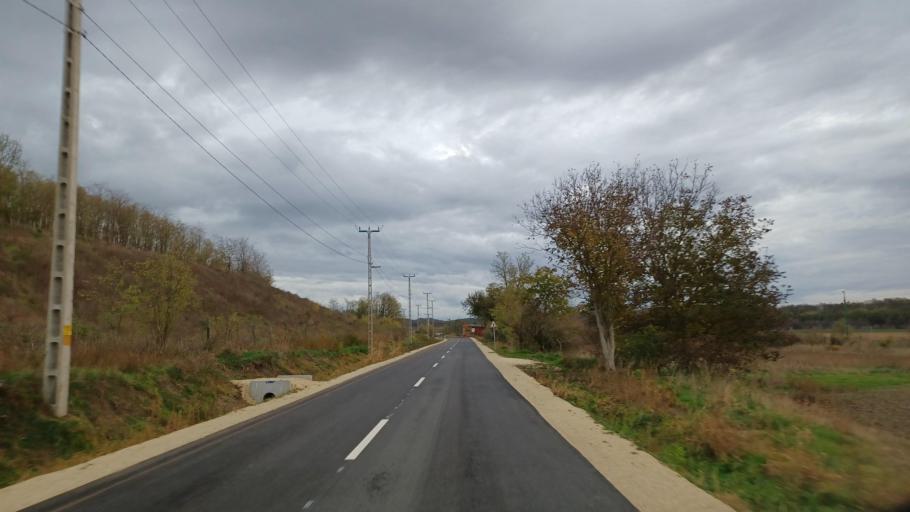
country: HU
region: Tolna
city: Gyonk
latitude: 46.6021
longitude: 18.4244
